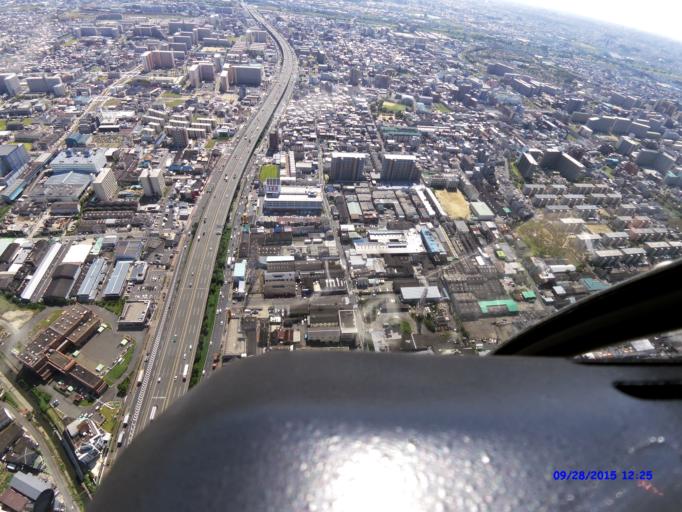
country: JP
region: Osaka
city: Yao
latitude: 34.6171
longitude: 135.5736
